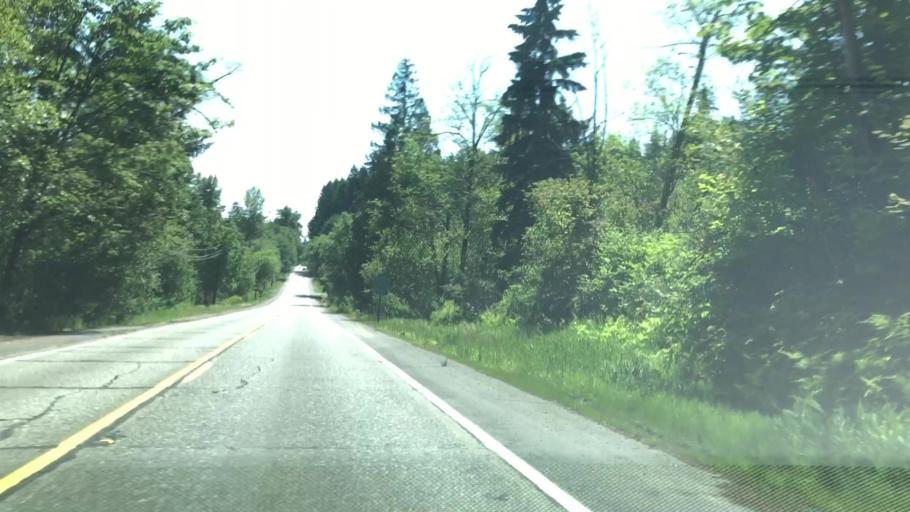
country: US
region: Washington
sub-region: King County
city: Cottage Lake
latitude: 47.7261
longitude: -122.0846
